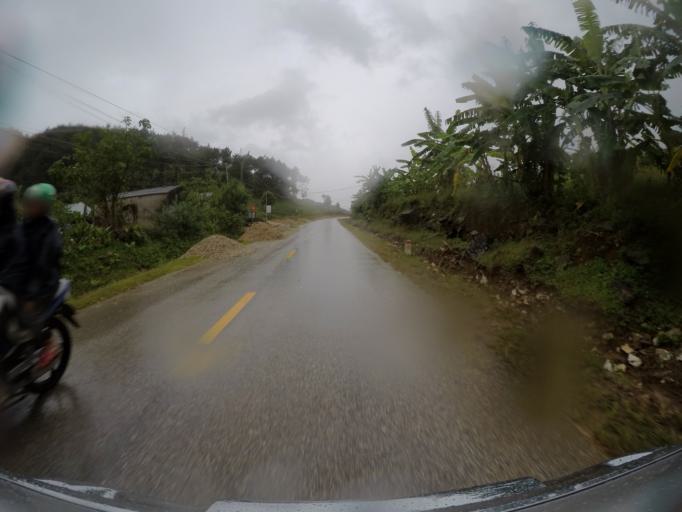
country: VN
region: Lai Chau
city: Than Uyen
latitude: 22.0561
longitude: 103.9010
